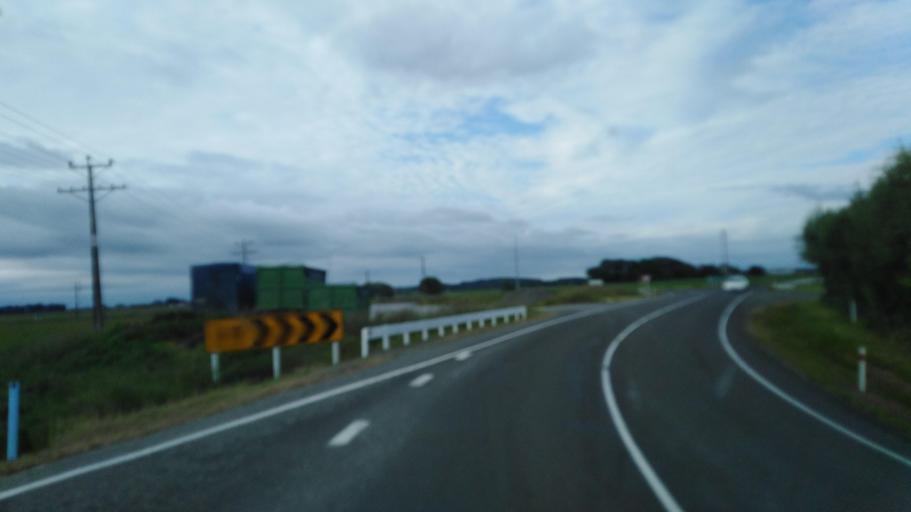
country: NZ
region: Manawatu-Wanganui
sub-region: Rangitikei District
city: Bulls
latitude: -40.1245
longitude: 175.3545
